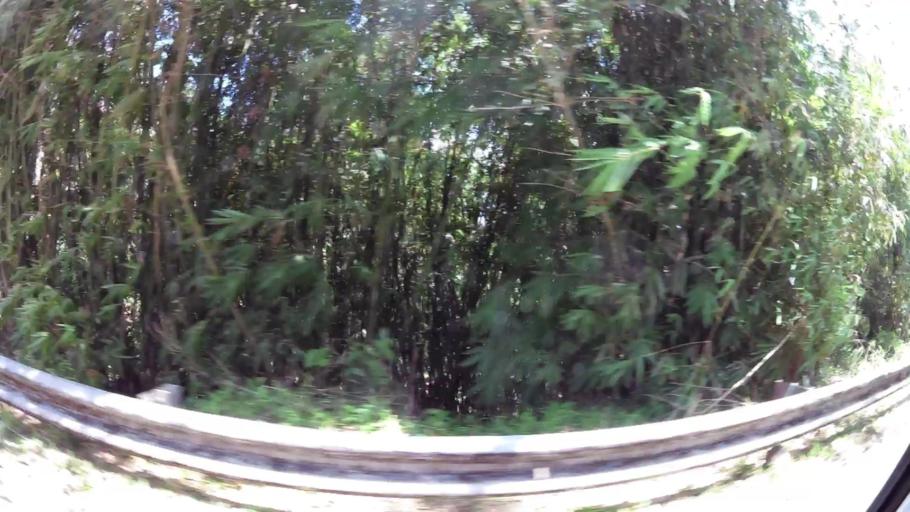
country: BN
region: Brunei and Muara
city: Bandar Seri Begawan
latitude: 4.9371
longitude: 114.9702
